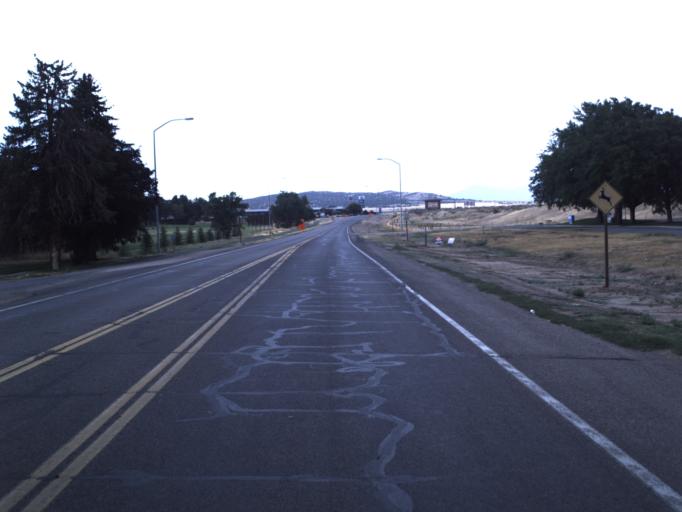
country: US
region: Utah
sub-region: Millard County
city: Fillmore
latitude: 38.9827
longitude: -112.3237
